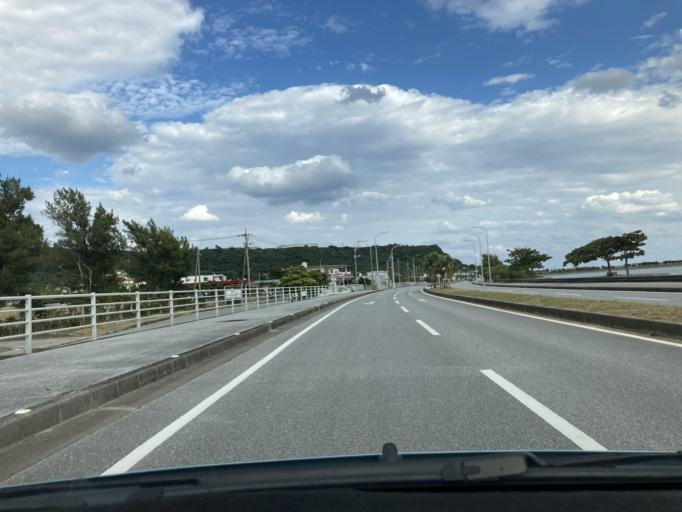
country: JP
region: Okinawa
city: Katsuren-haebaru
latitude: 26.3402
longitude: 127.9472
